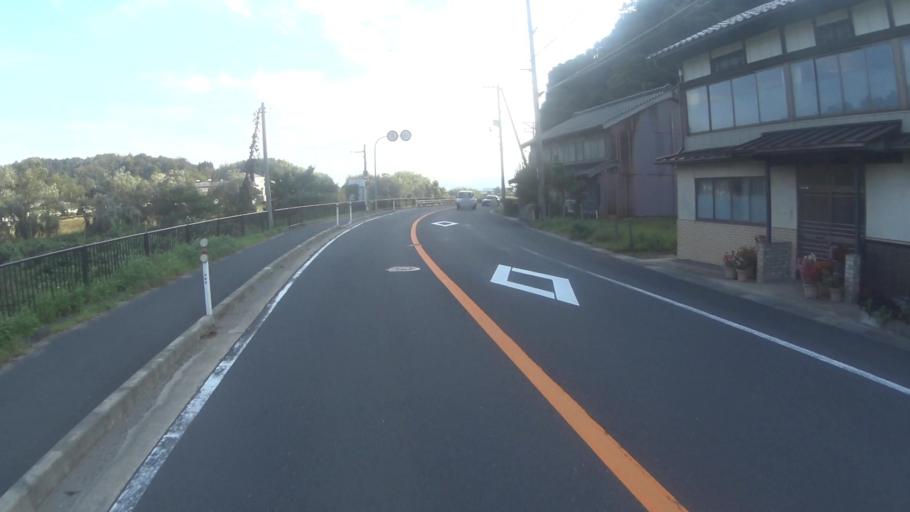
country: JP
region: Kyoto
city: Miyazu
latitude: 35.6371
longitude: 135.0802
